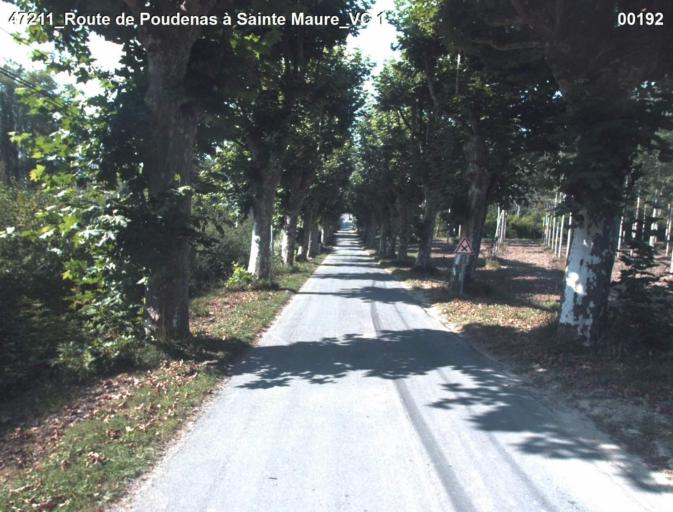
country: FR
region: Aquitaine
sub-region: Departement du Lot-et-Garonne
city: Mezin
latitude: 44.0435
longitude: 0.2108
